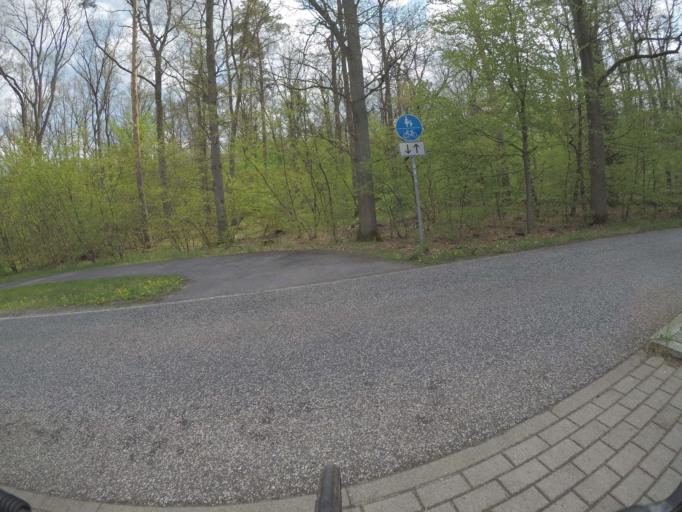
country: DE
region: Brandenburg
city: Marienwerder
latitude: 52.8851
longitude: 13.6372
